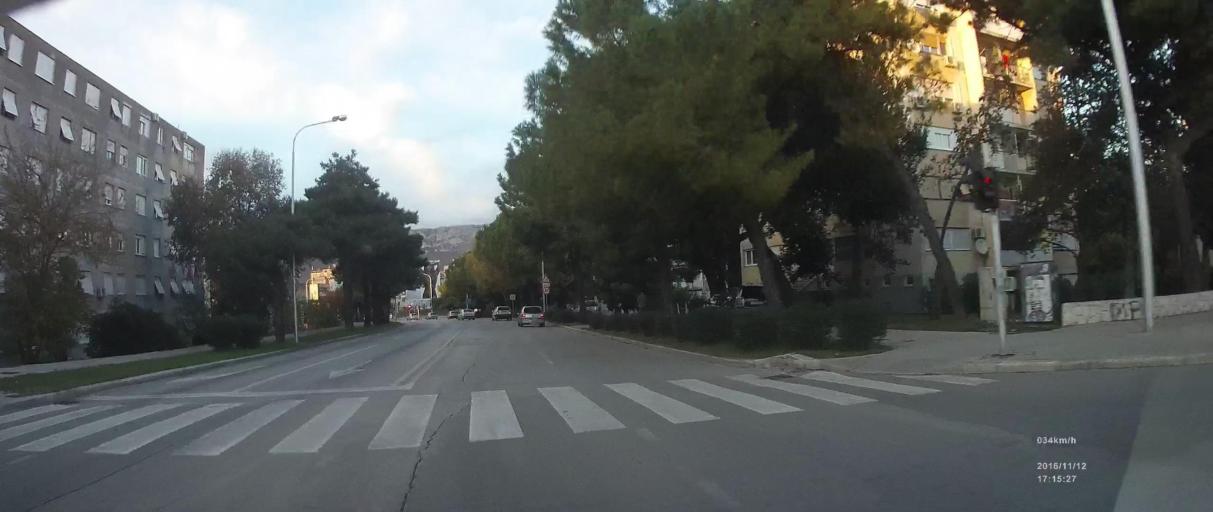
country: HR
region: Splitsko-Dalmatinska
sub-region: Grad Split
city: Split
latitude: 43.5132
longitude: 16.4492
